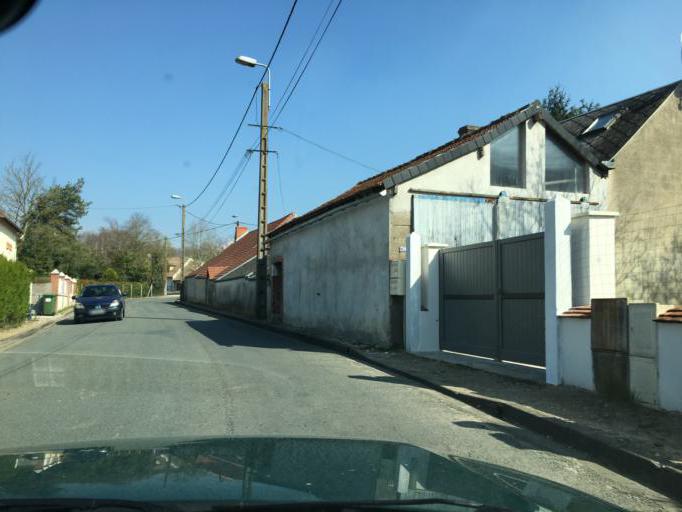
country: FR
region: Centre
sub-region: Departement du Loiret
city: Saran
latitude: 47.9534
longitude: 1.9004
